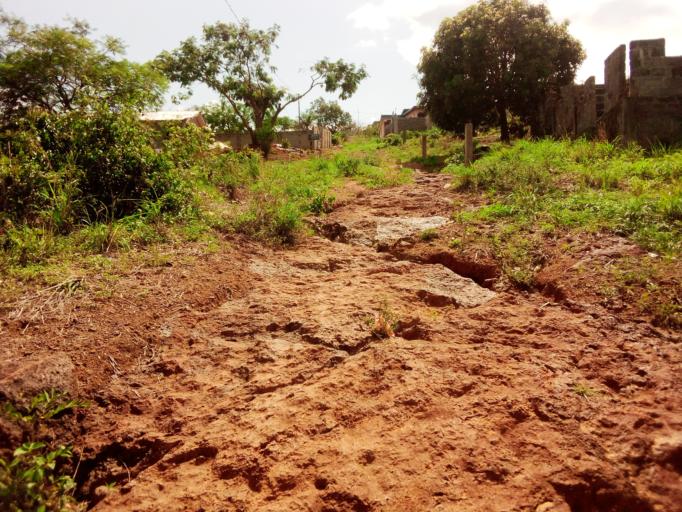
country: SL
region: Western Area
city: Waterloo
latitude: 8.3419
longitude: -13.0761
